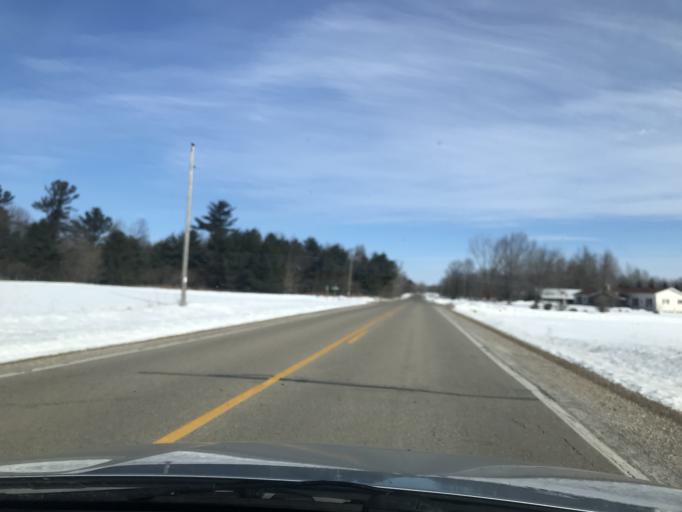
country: US
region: Wisconsin
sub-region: Oconto County
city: Oconto Falls
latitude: 44.9220
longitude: -88.1547
